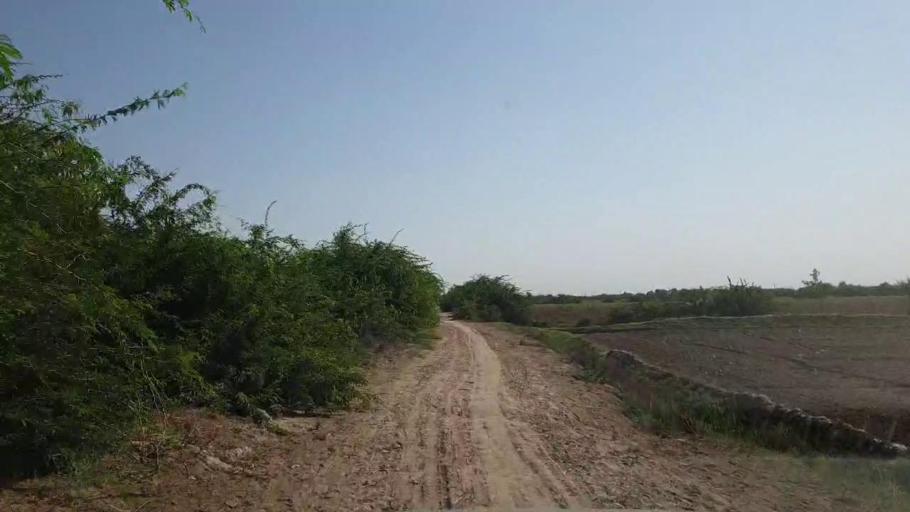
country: PK
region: Sindh
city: Kadhan
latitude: 24.5899
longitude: 69.0086
